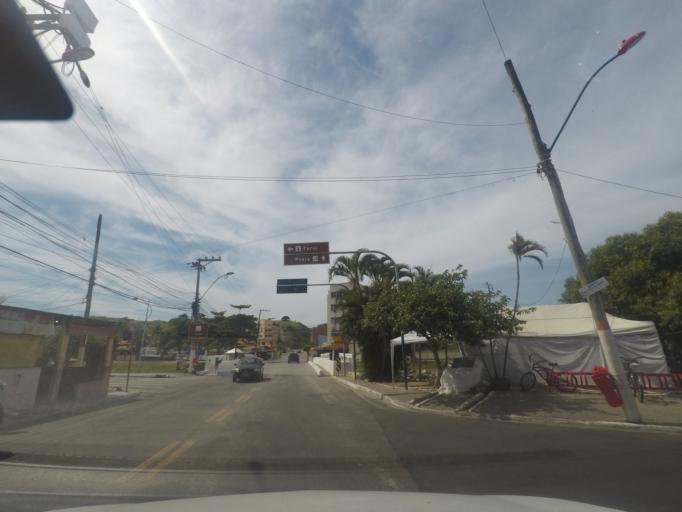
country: BR
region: Rio de Janeiro
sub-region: Marica
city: Marica
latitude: -22.9542
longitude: -42.6961
